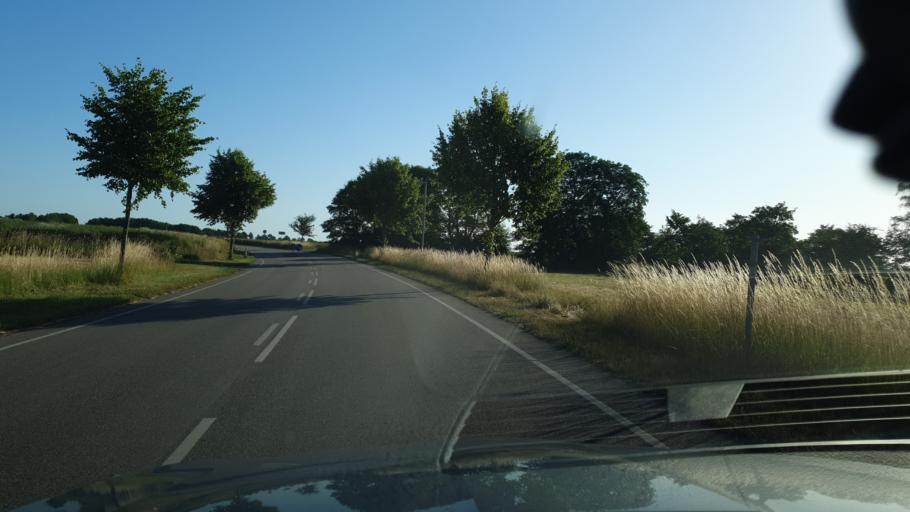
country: DK
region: Zealand
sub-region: Soro Kommune
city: Frederiksberg
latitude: 55.4012
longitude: 11.5628
